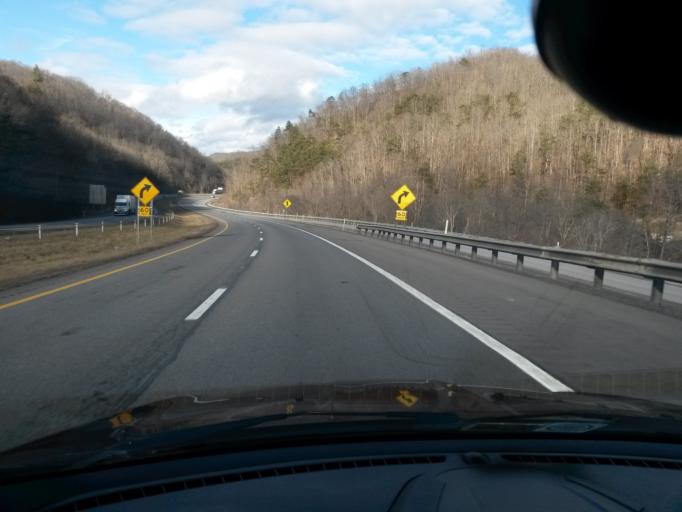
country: US
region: West Virginia
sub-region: Mercer County
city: Princeton
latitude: 37.3150
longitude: -81.0592
